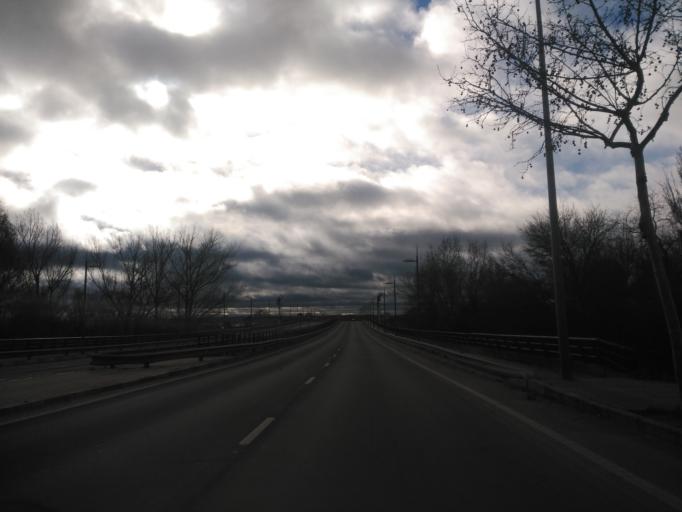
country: ES
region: Castille and Leon
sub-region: Provincia de Zamora
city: Zamora
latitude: 41.5044
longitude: -5.7318
